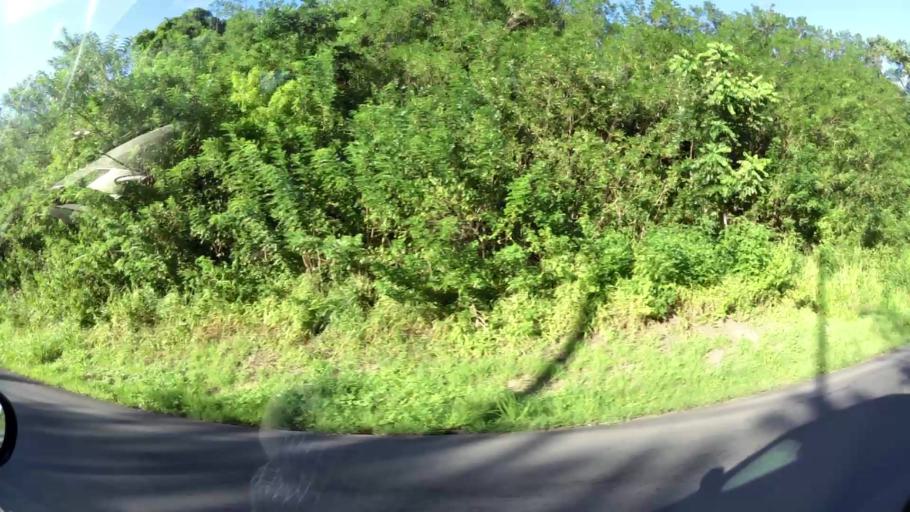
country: TT
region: Tobago
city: Scarborough
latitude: 11.2114
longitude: -60.7644
